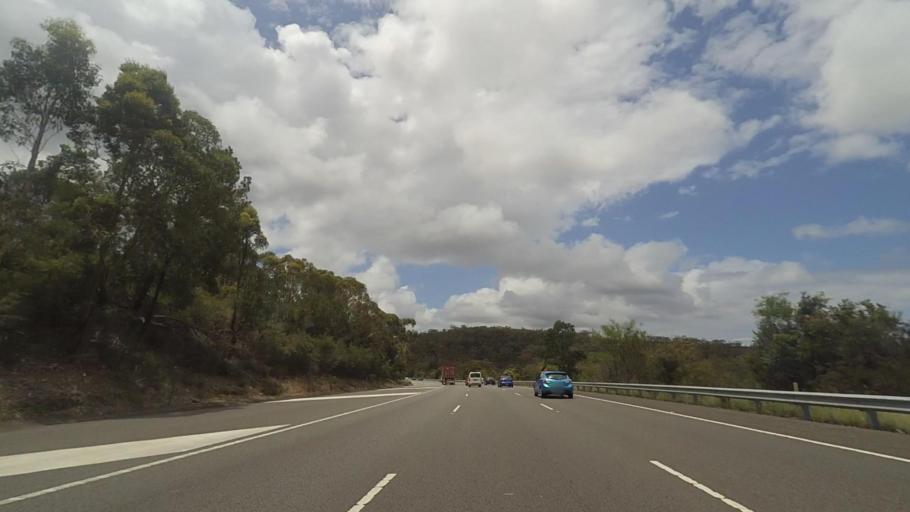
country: AU
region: New South Wales
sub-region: Gosford Shire
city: Point Clare
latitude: -33.4503
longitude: 151.2162
